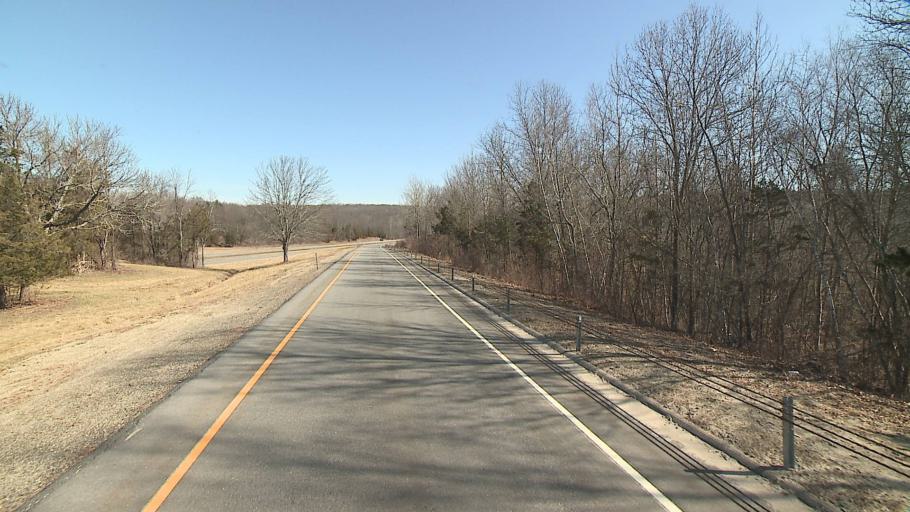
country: US
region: Connecticut
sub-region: New London County
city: Montville Center
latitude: 41.5693
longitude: -72.2074
